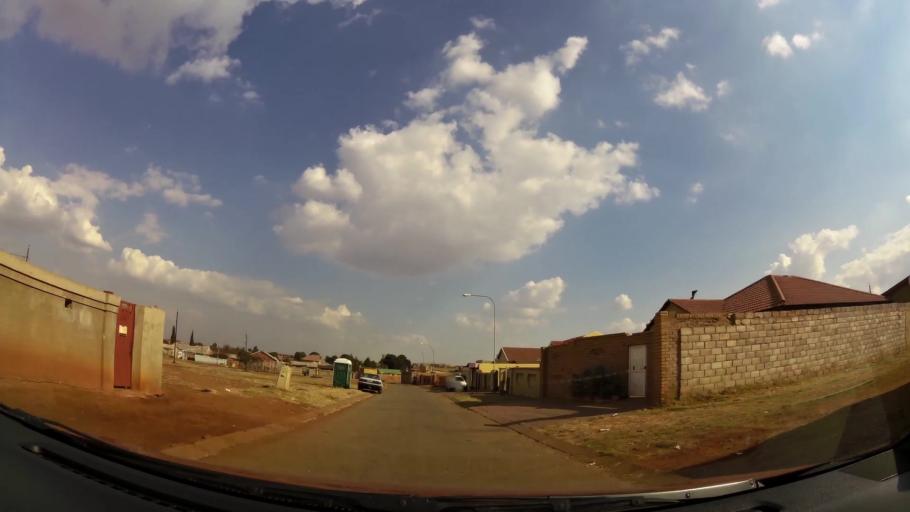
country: ZA
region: Gauteng
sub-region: City of Johannesburg Metropolitan Municipality
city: Soweto
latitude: -26.2188
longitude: 27.8619
